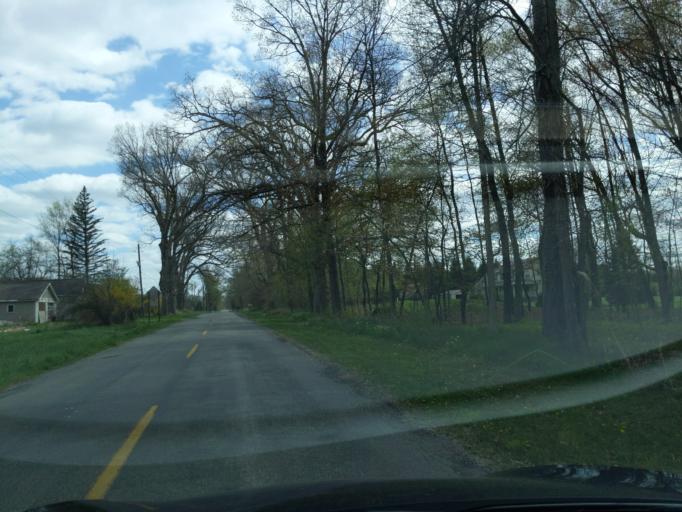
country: US
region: Michigan
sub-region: Eaton County
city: Eaton Rapids
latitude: 42.5086
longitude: -84.5464
